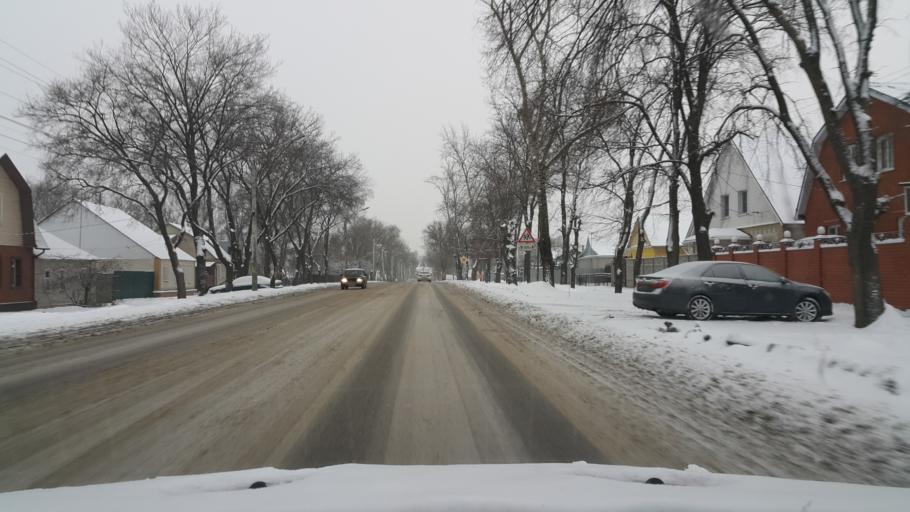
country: RU
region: Tambov
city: Pokrovo-Prigorodnoye
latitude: 52.7025
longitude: 41.4293
